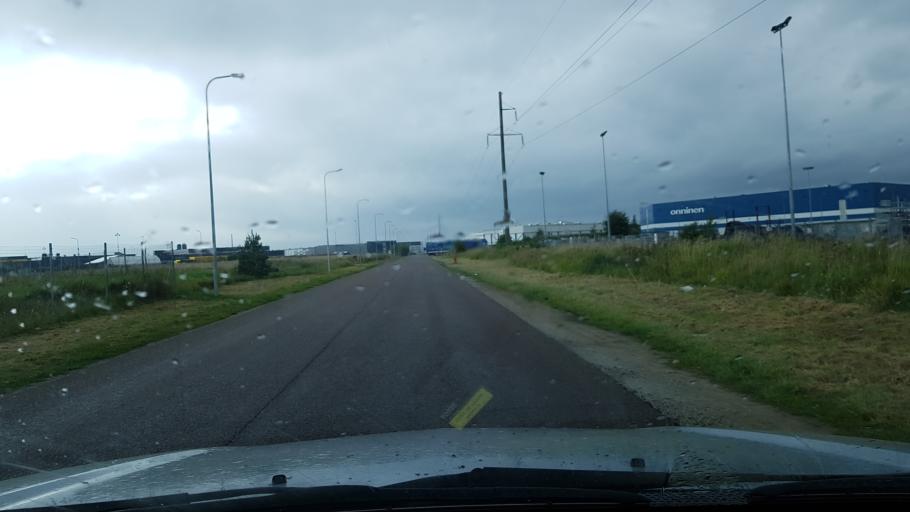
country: EE
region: Harju
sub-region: Rae vald
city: Jueri
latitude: 59.3630
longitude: 24.8964
